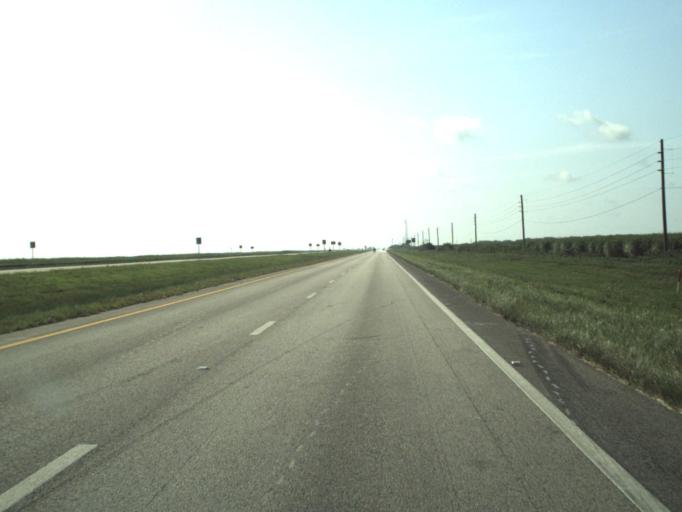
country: US
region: Florida
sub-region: Palm Beach County
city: Belle Glade Camp
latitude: 26.5281
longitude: -80.6877
